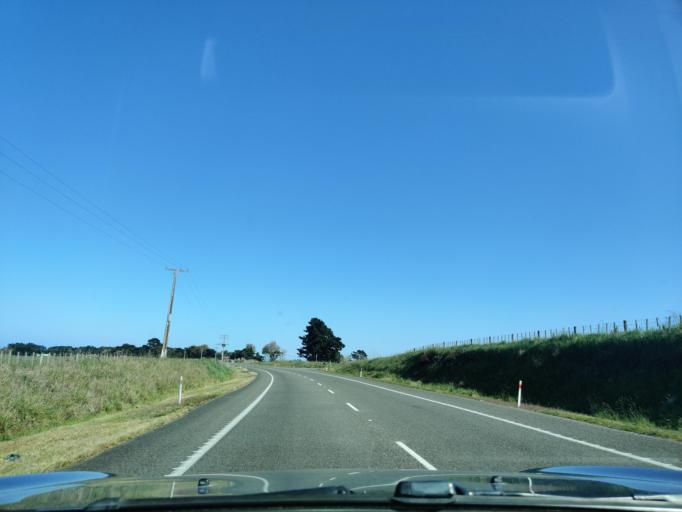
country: NZ
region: Manawatu-Wanganui
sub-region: Wanganui District
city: Wanganui
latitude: -39.9757
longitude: 175.1302
